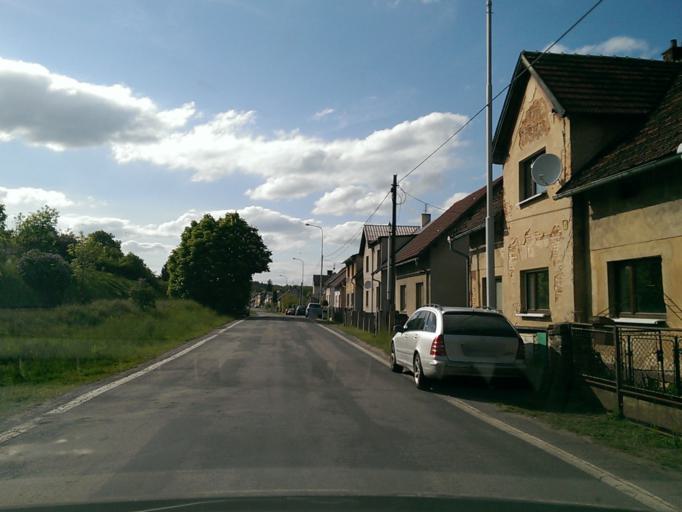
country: CZ
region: Central Bohemia
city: Bakov nad Jizerou
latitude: 50.4895
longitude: 14.9201
